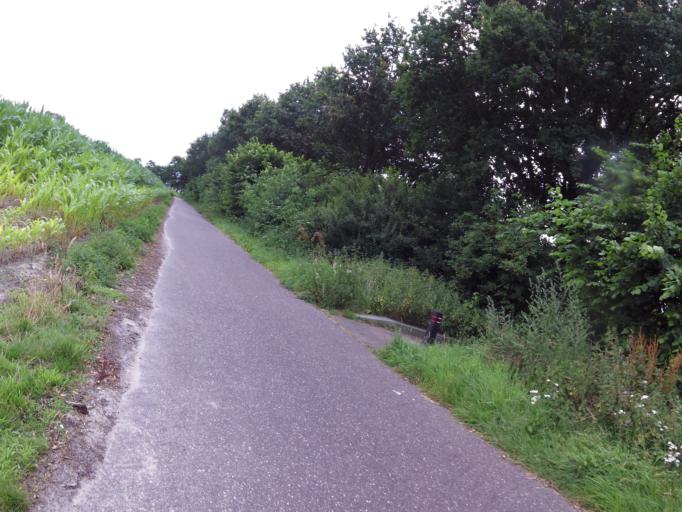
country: NL
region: North Brabant
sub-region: Gemeente Sint-Oedenrode
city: Sint-Oedenrode
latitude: 51.5581
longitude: 5.4826
